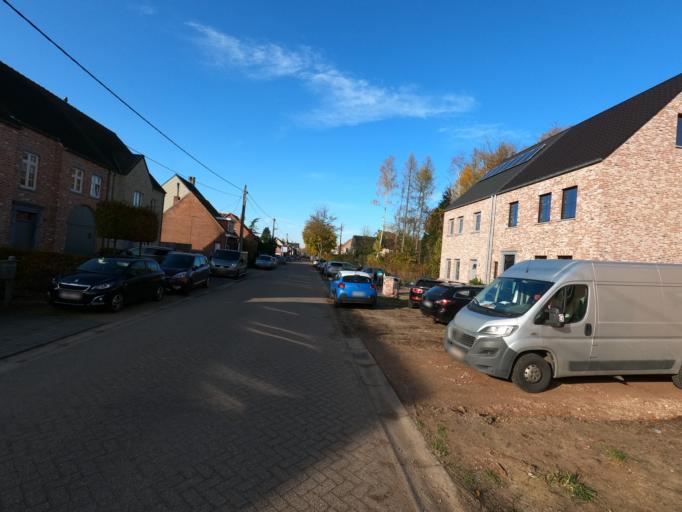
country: BE
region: Flanders
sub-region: Provincie Antwerpen
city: Wuustwezel
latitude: 51.3505
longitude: 4.5487
